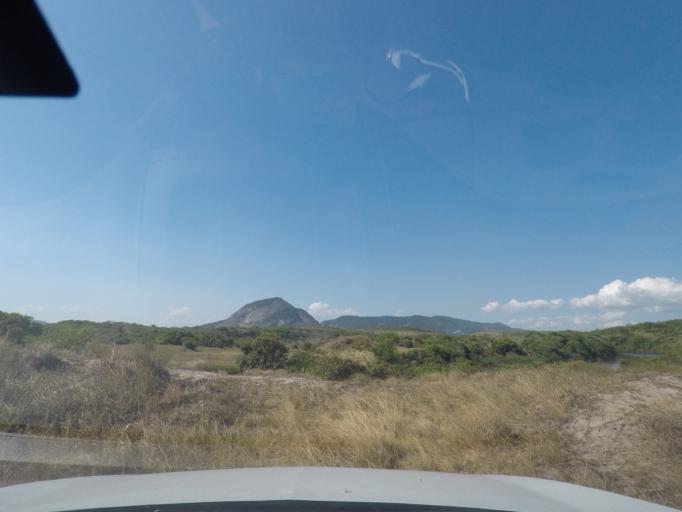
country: BR
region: Rio de Janeiro
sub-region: Marica
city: Marica
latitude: -22.9644
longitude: -42.9044
